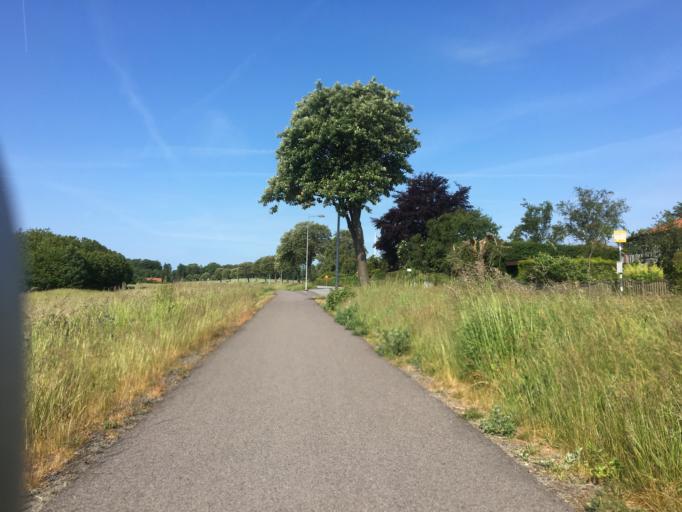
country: SE
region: Skane
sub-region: Ystads Kommun
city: Ystad
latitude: 55.4267
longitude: 13.7091
